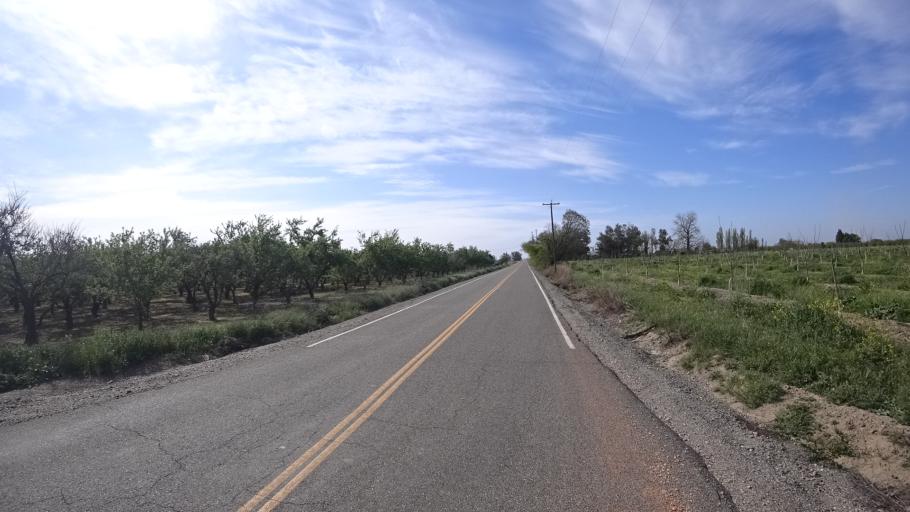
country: US
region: California
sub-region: Glenn County
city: Hamilton City
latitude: 39.6305
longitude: -122.0368
